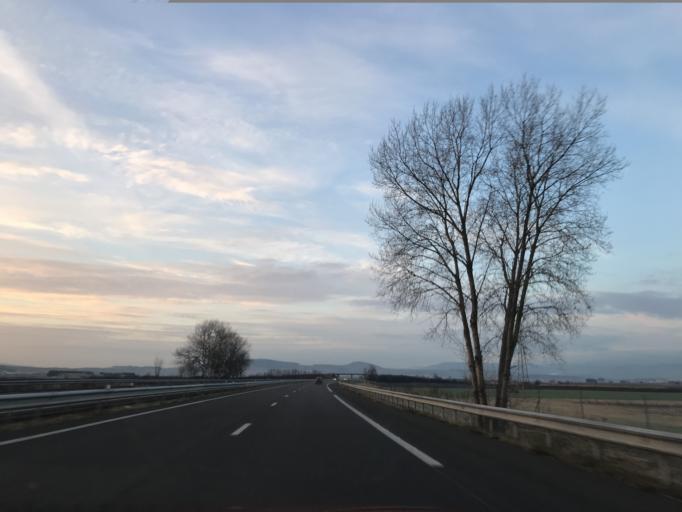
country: FR
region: Auvergne
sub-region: Departement du Puy-de-Dome
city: Pont-du-Chateau
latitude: 45.8090
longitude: 3.2205
